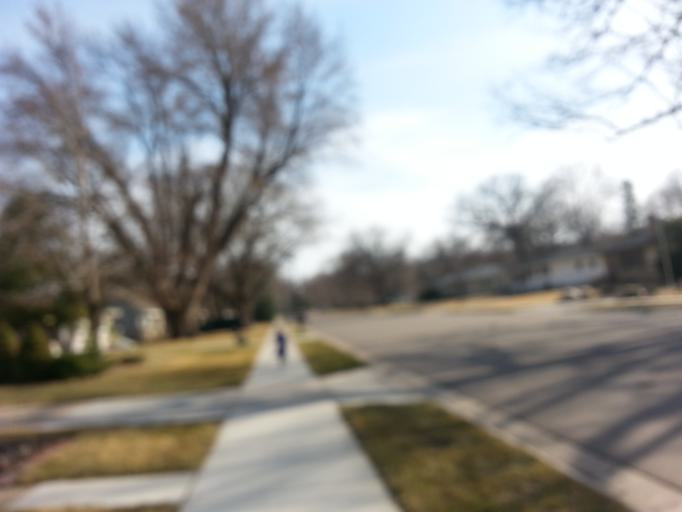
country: US
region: Minnesota
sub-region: Scott County
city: Savage
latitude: 44.7745
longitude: -93.3369
